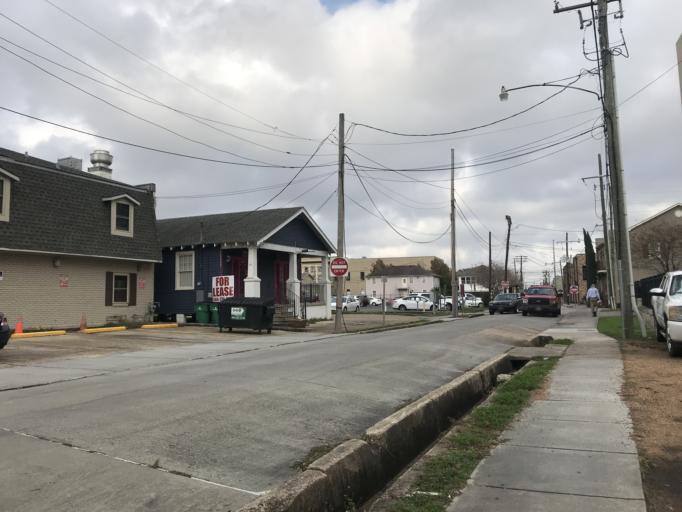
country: US
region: Louisiana
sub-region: Jefferson Parish
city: Gretna
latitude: 29.9156
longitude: -90.0666
